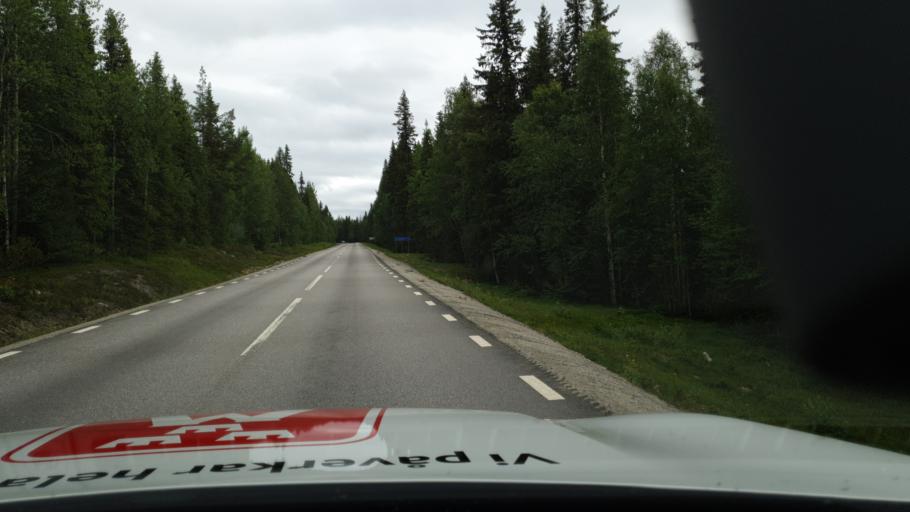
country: SE
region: Vaesterbotten
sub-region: Asele Kommun
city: Insjon
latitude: 64.7192
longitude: 17.6648
